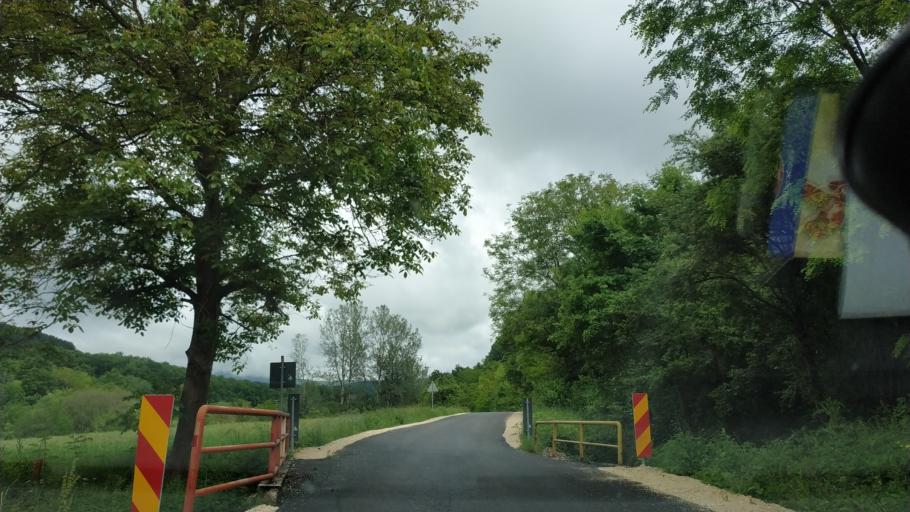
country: RS
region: Central Serbia
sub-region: Zajecarski Okrug
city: Soko Banja
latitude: 43.6623
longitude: 21.9102
